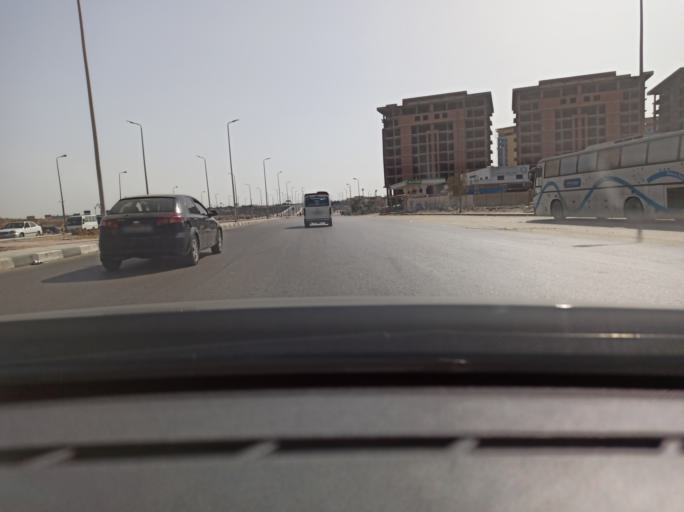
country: EG
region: Muhafazat al Qahirah
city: Cairo
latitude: 30.0515
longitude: 31.4017
